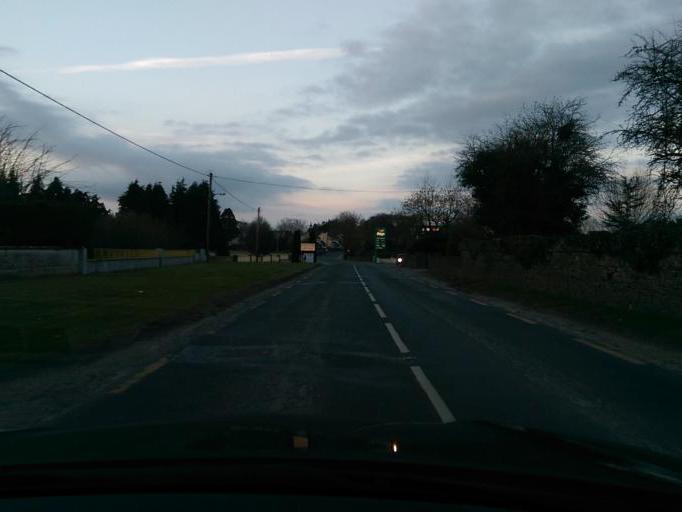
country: IE
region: Munster
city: Nenagh Bridge
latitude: 52.9875
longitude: -8.1325
